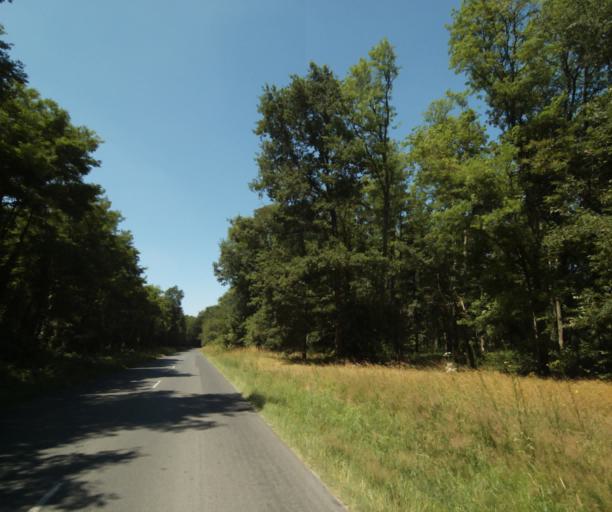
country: FR
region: Ile-de-France
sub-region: Departement de Seine-et-Marne
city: Noisy-sur-Ecole
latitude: 48.3720
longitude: 2.5082
